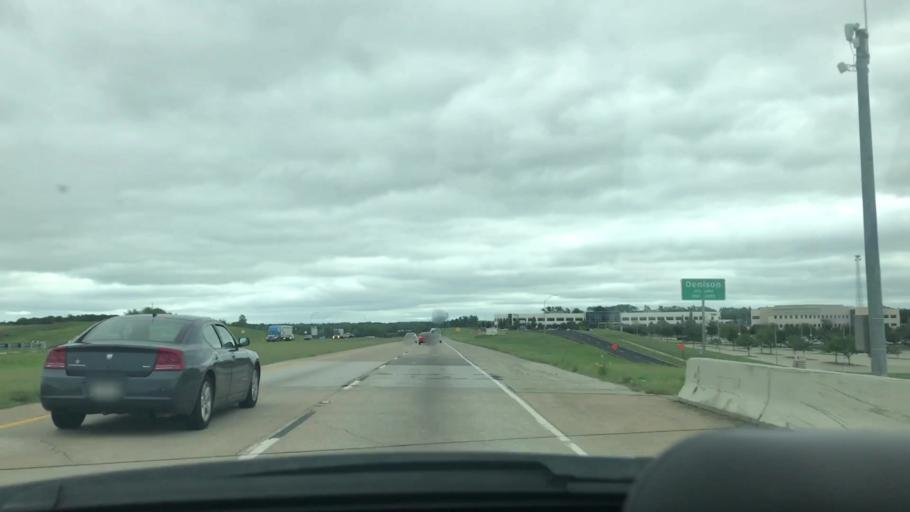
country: US
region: Texas
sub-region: Grayson County
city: Denison
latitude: 33.7084
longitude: -96.5893
